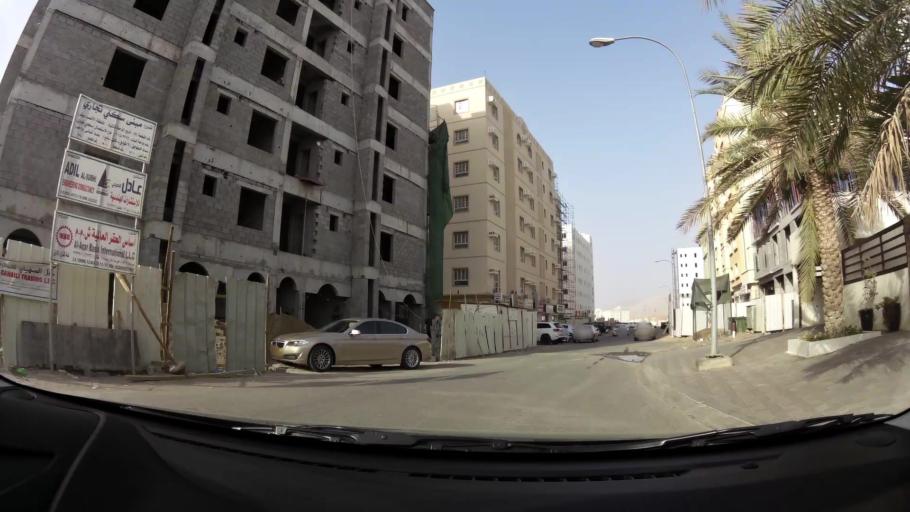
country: OM
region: Muhafazat Masqat
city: Bawshar
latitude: 23.5459
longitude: 58.3557
